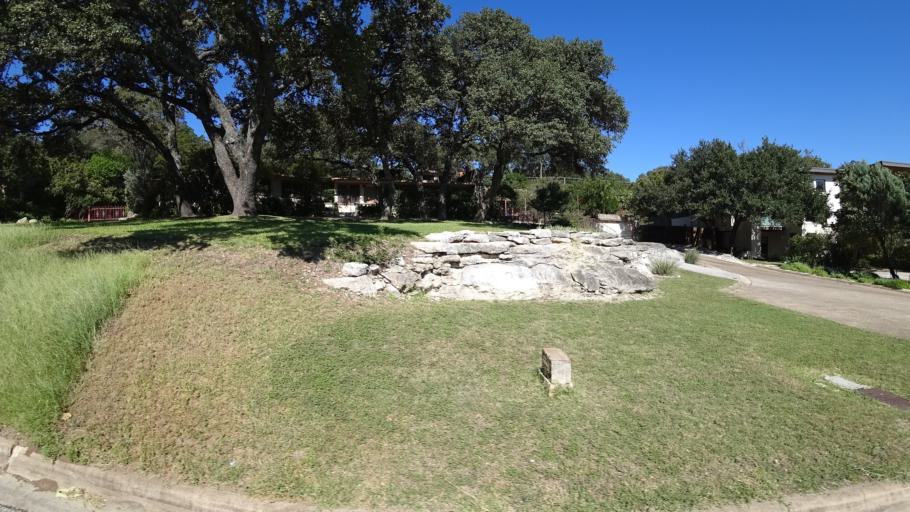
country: US
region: Texas
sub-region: Travis County
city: West Lake Hills
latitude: 30.3320
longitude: -97.7627
